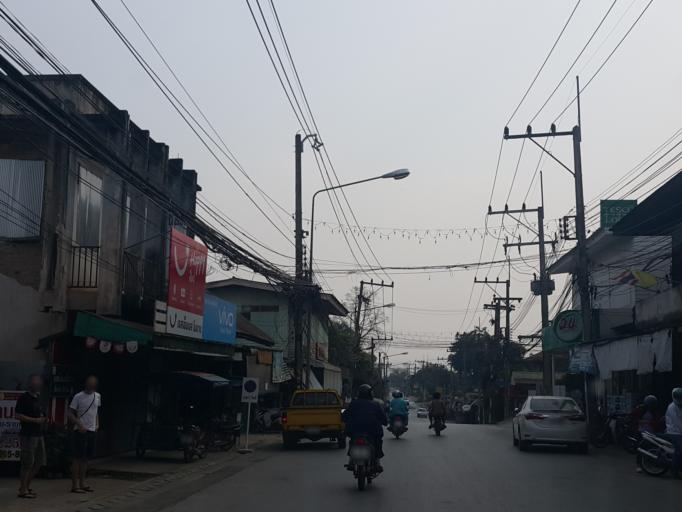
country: TH
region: Chiang Mai
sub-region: Amphoe Chiang Dao
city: Chiang Dao
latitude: 19.3681
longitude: 98.9650
